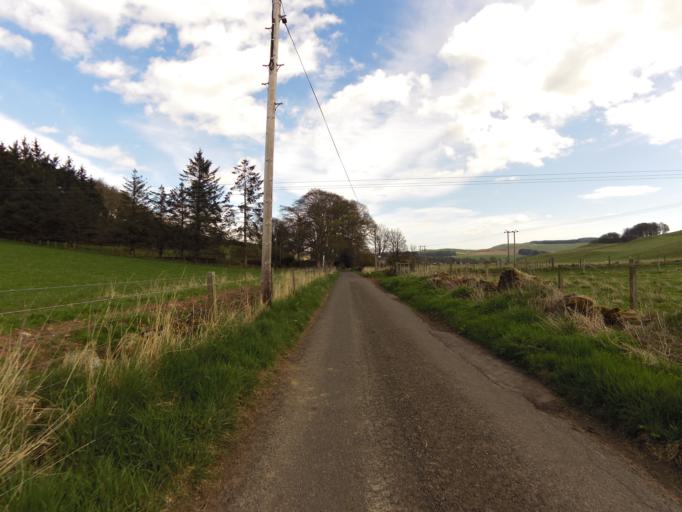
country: GB
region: Scotland
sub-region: Fife
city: Newburgh
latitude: 56.3351
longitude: -3.2440
